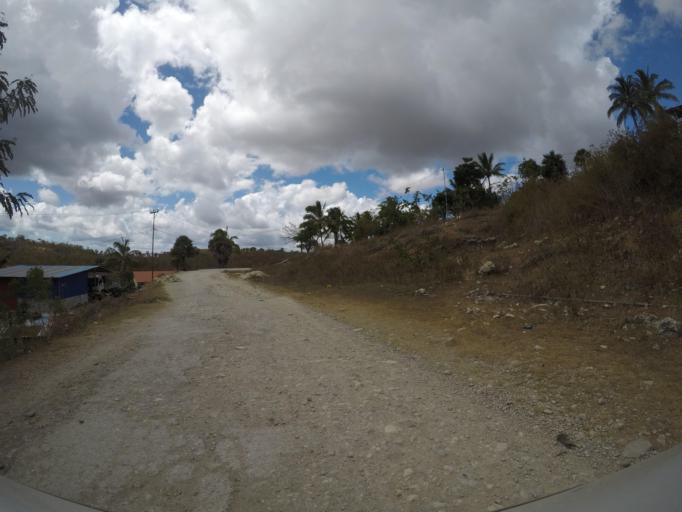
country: TL
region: Baucau
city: Baucau
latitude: -8.5193
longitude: 126.6923
